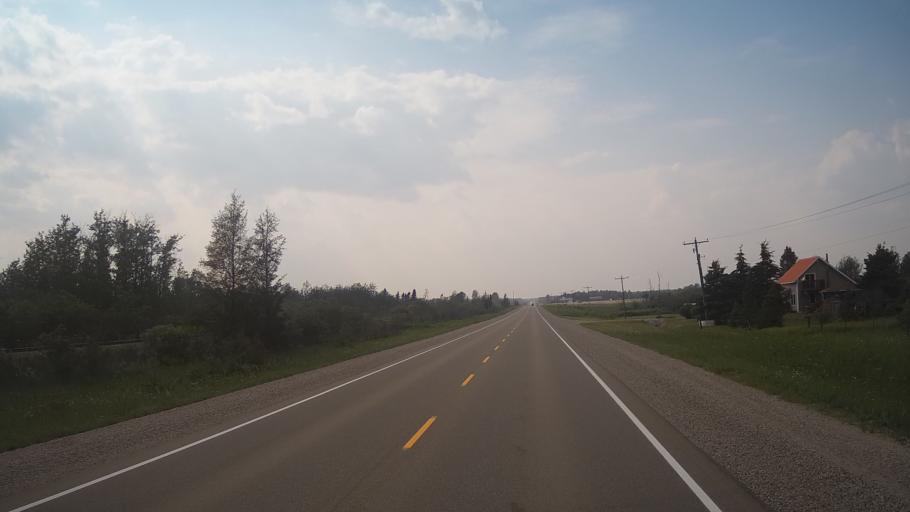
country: CA
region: Ontario
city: Kapuskasing
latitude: 49.4839
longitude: -82.7069
